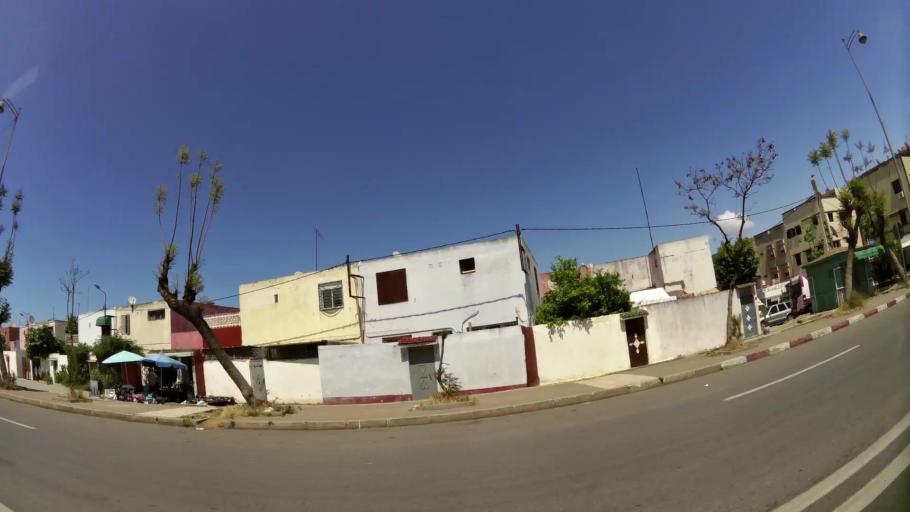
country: MA
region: Gharb-Chrarda-Beni Hssen
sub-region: Kenitra Province
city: Kenitra
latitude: 34.2479
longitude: -6.5543
